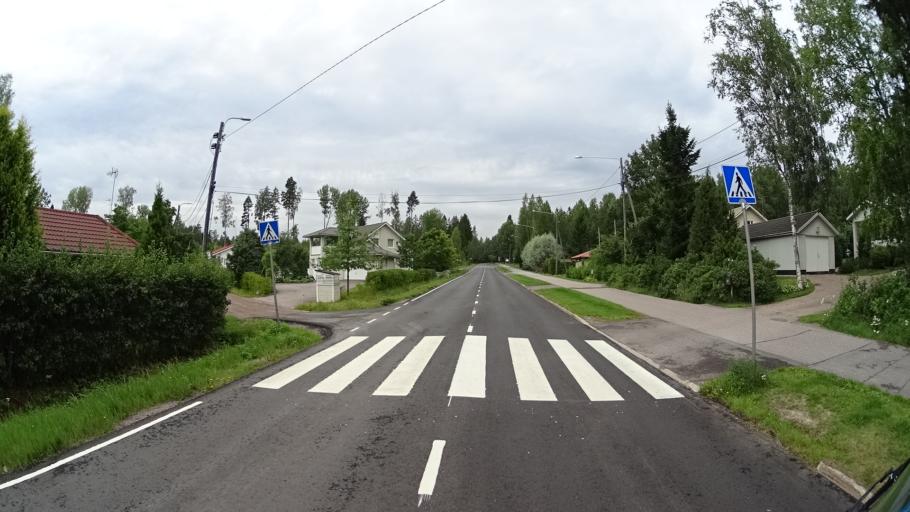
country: FI
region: Uusimaa
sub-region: Helsinki
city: Kilo
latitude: 60.2402
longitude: 24.7662
